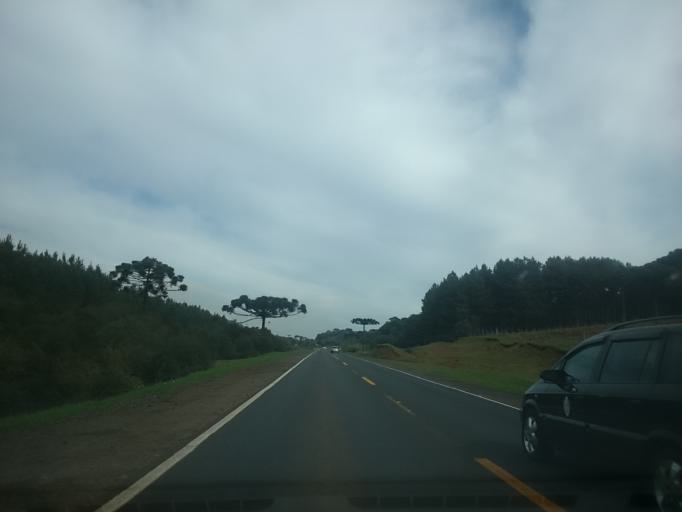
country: BR
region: Santa Catarina
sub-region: Lages
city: Lages
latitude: -28.0509
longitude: -50.5684
